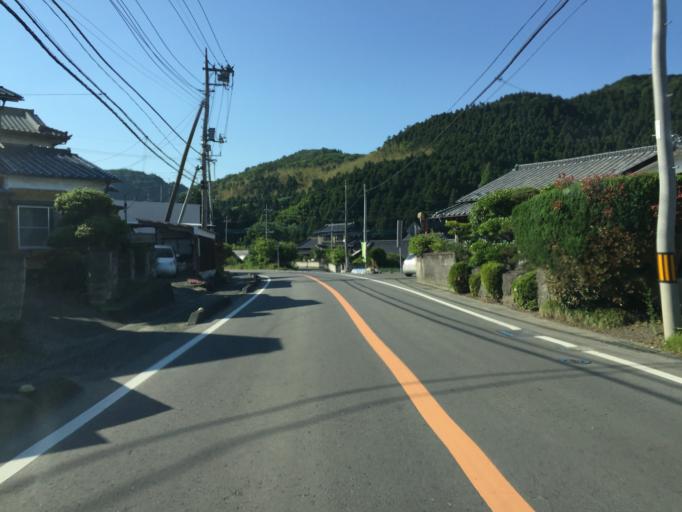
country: JP
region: Ibaraki
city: Kitaibaraki
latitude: 36.8565
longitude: 140.7277
